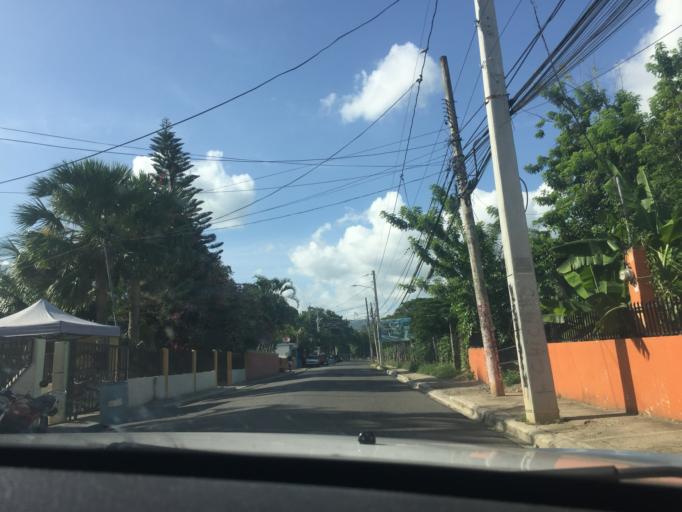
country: DO
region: Santiago
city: Tamboril
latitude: 19.4832
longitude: -70.6551
